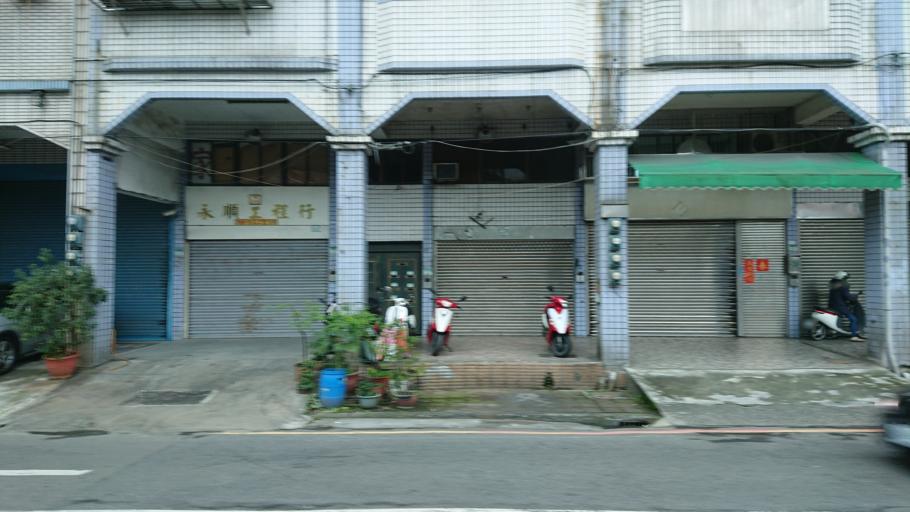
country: TW
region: Taiwan
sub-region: Taoyuan
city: Taoyuan
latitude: 24.9570
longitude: 121.3518
